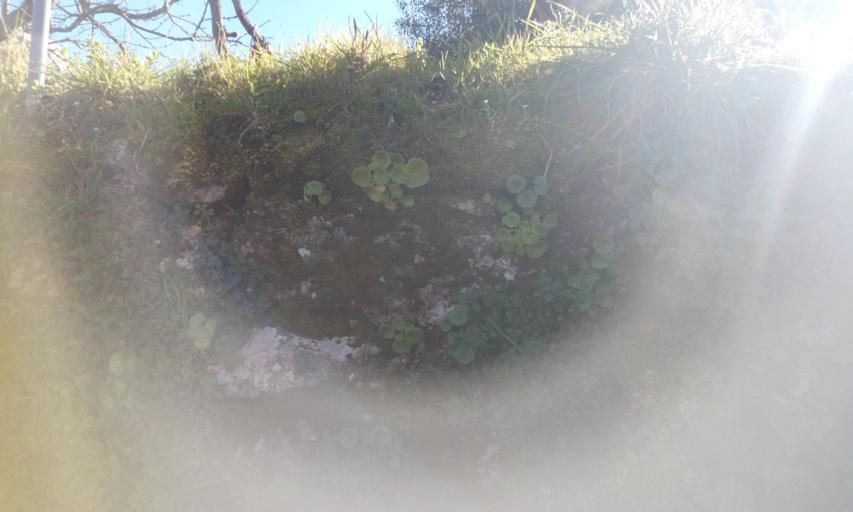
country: PT
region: Guarda
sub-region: Manteigas
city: Manteigas
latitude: 40.4648
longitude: -7.6065
